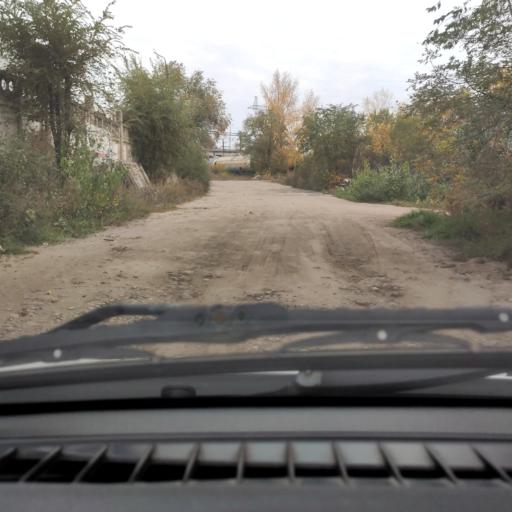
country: RU
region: Samara
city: Zhigulevsk
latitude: 53.4859
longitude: 49.4994
